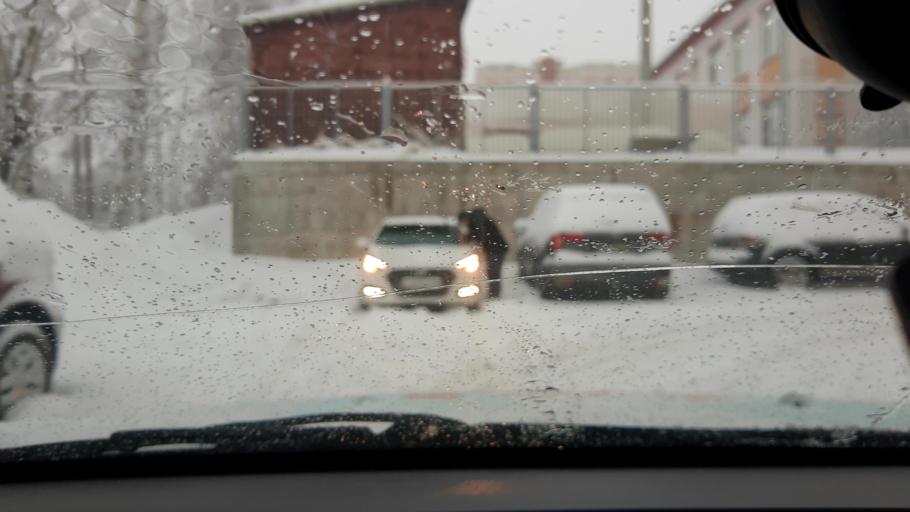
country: RU
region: Nizjnij Novgorod
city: Kstovo
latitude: 56.1593
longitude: 44.2187
